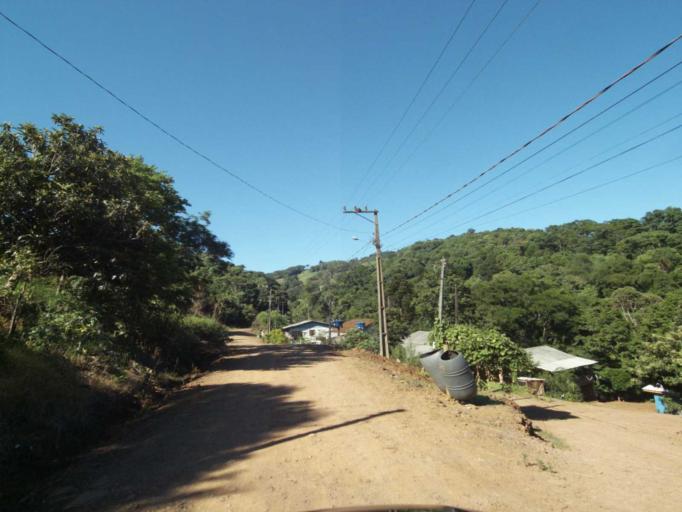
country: BR
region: Parana
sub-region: Francisco Beltrao
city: Francisco Beltrao
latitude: -26.1457
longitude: -53.3128
